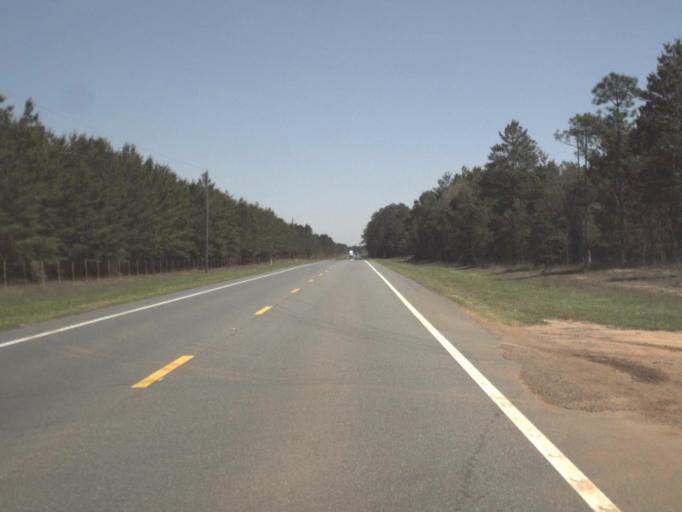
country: US
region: Florida
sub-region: Bay County
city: Youngstown
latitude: 30.4338
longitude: -85.2602
